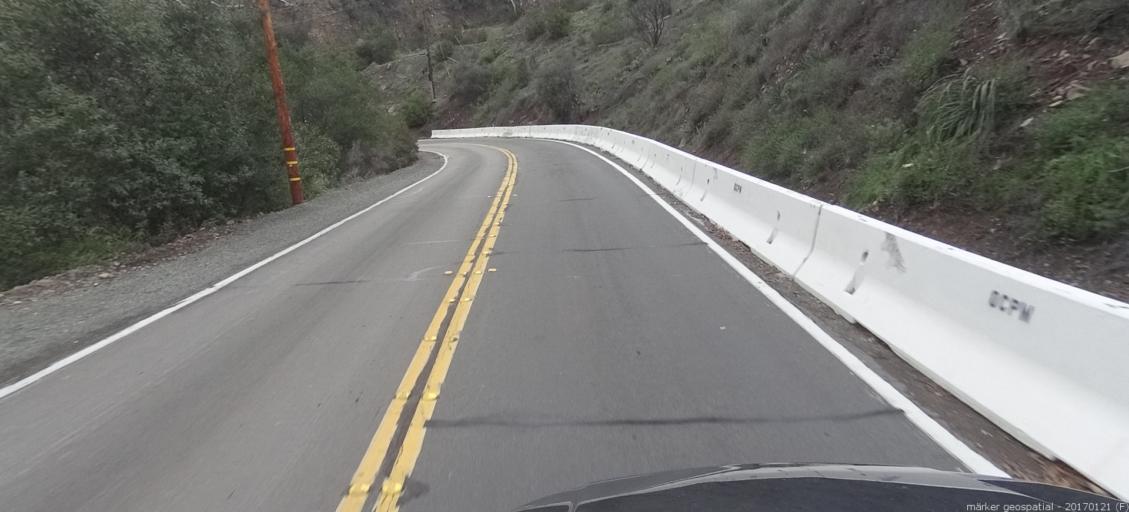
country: US
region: California
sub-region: Orange County
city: Portola Hills
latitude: 33.7463
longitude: -117.5992
